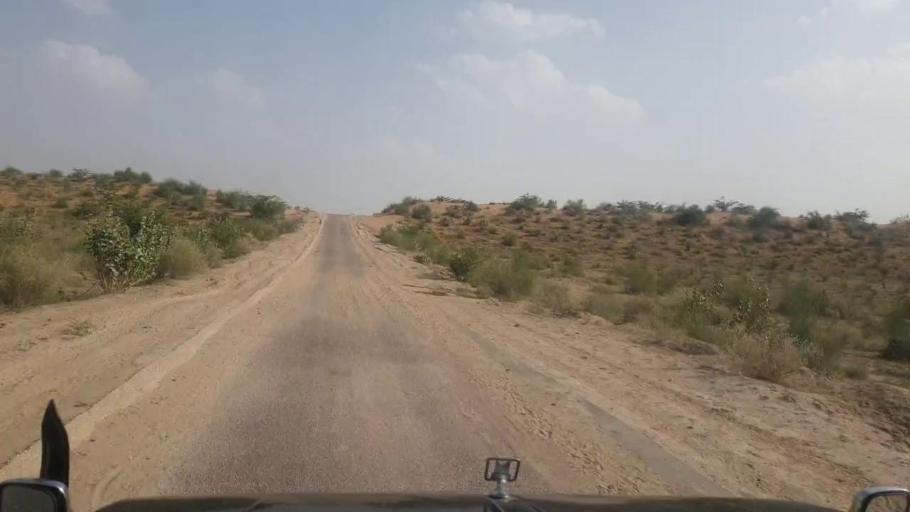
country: PK
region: Sindh
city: Islamkot
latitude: 25.1413
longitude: 70.3164
